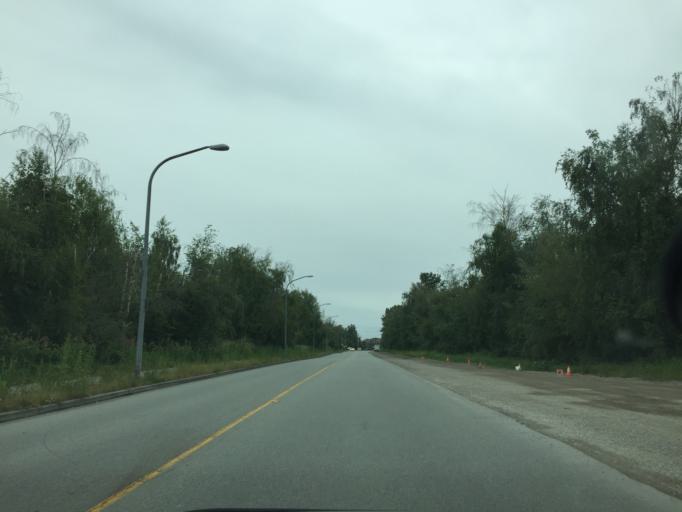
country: CA
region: British Columbia
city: Richmond
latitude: 49.1736
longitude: -123.1030
